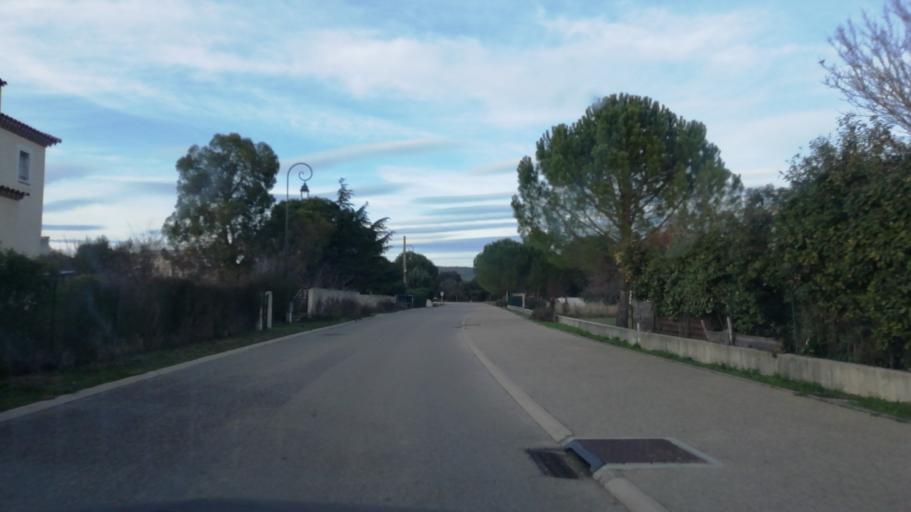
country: FR
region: Languedoc-Roussillon
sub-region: Departement de l'Herault
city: Claret
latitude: 43.8394
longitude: 3.9190
